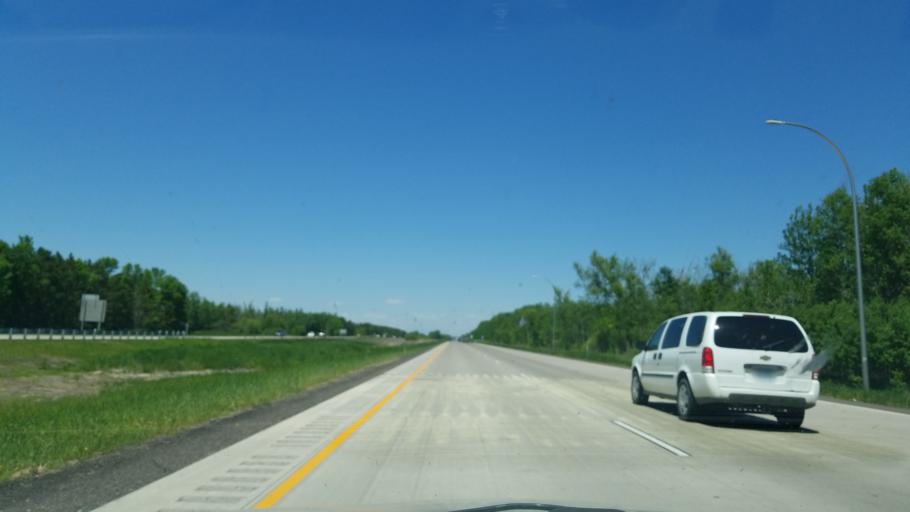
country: US
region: Minnesota
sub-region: Pine County
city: Pine City
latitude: 45.9075
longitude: -92.9667
